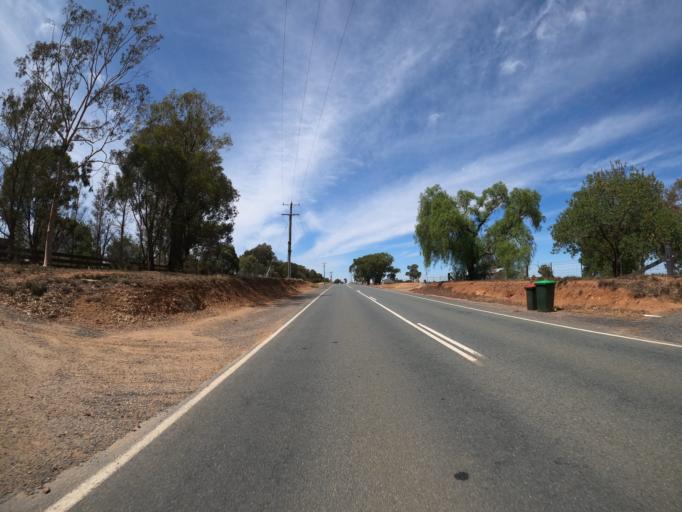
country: AU
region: Victoria
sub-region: Moira
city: Yarrawonga
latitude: -36.0450
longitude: 145.9955
